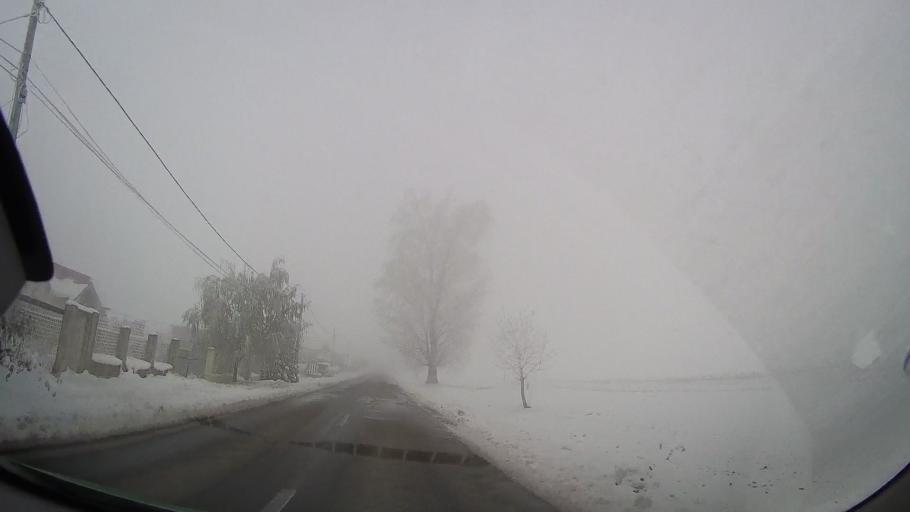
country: RO
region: Neamt
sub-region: Comuna Sabaoani
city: Sabaoani
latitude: 47.0268
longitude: 26.8607
